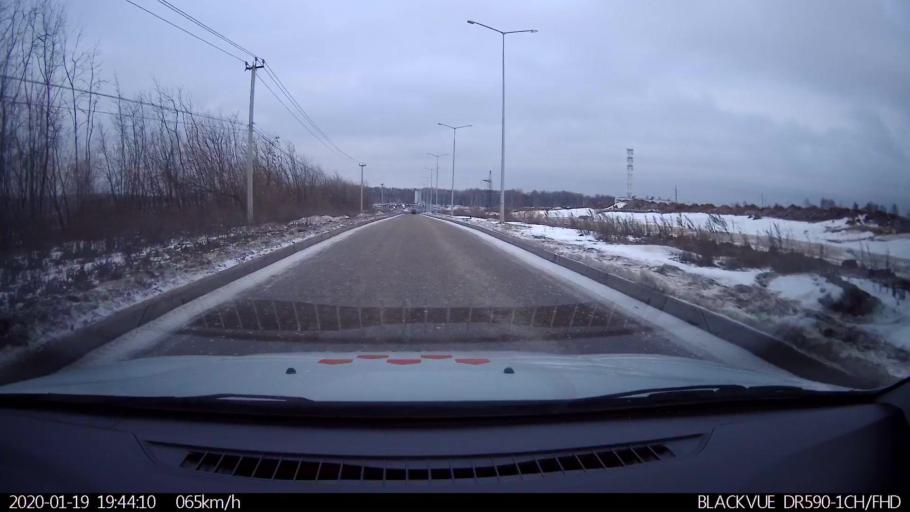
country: RU
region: Nizjnij Novgorod
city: Afonino
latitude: 56.2472
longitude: 44.0545
